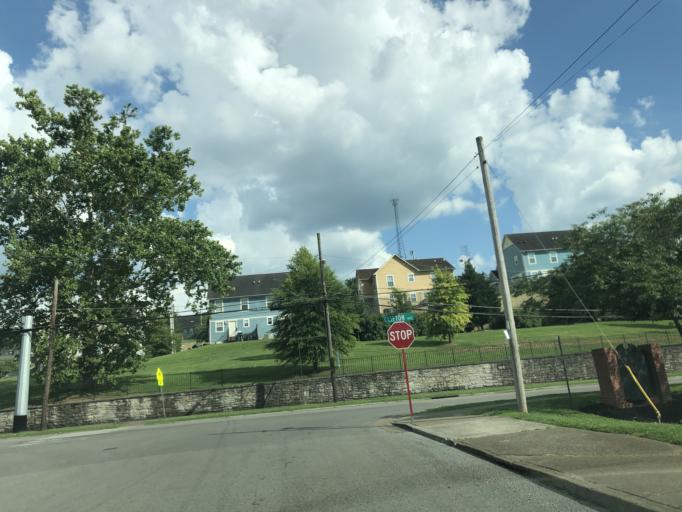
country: US
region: Tennessee
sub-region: Davidson County
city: Nashville
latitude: 36.1578
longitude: -86.8304
